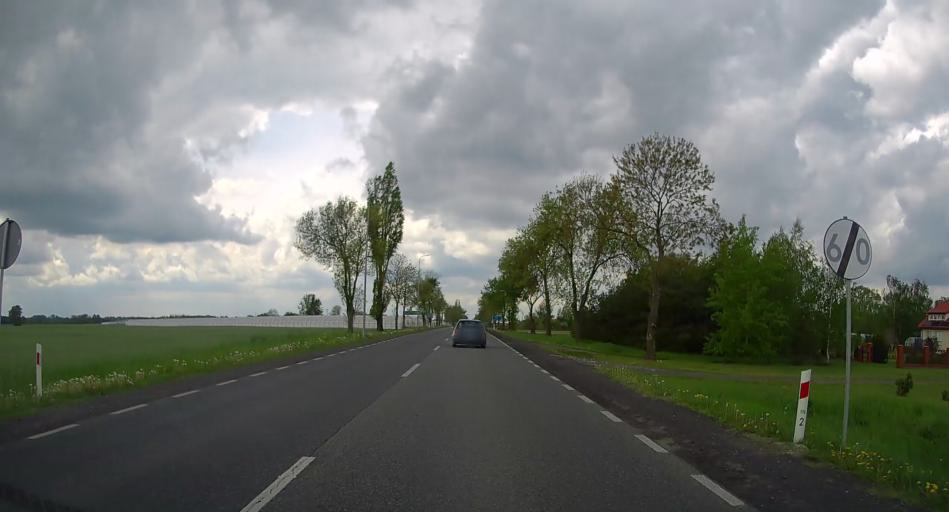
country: PL
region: Masovian Voivodeship
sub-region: Powiat plonski
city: Zaluski
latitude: 52.4419
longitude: 20.4882
